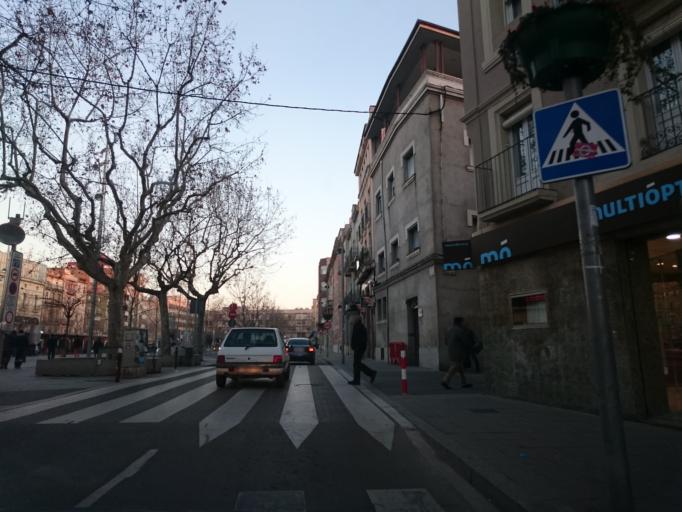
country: ES
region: Catalonia
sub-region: Provincia de Barcelona
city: Vilafranca del Penedes
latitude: 41.3457
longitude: 1.6973
